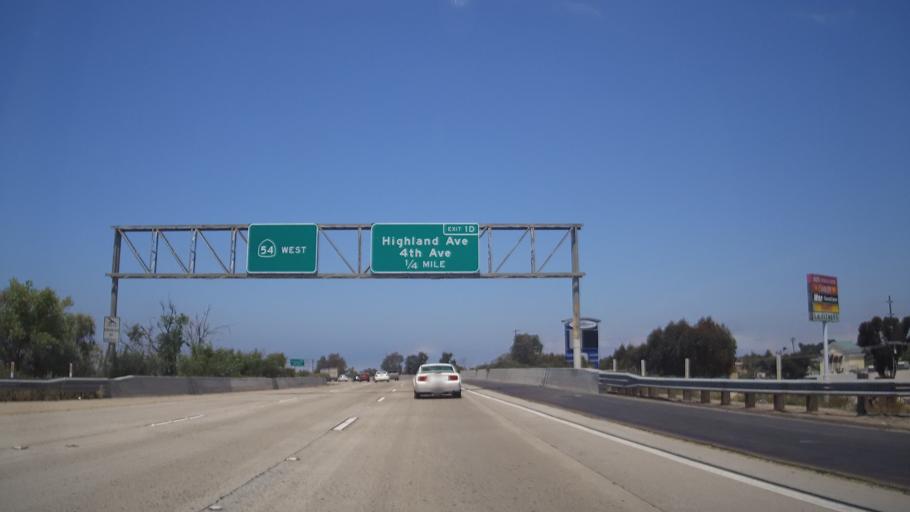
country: US
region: California
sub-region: San Diego County
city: Chula Vista
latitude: 32.6591
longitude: -117.0805
